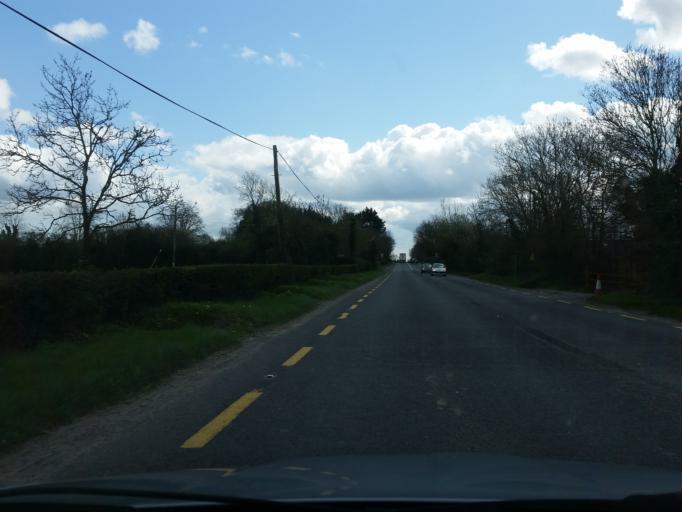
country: IE
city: Kentstown
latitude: 53.6523
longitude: -6.5172
